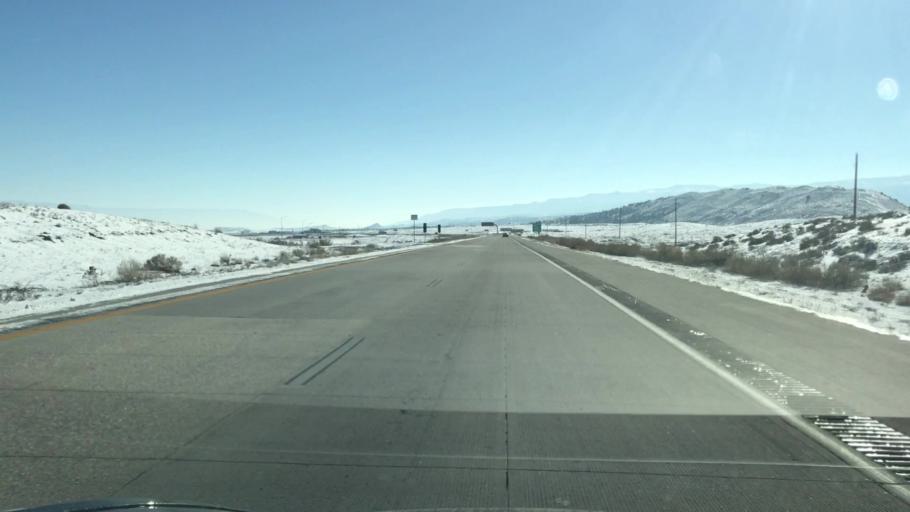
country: US
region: Colorado
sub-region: Mesa County
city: Loma
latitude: 39.1841
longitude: -108.8315
